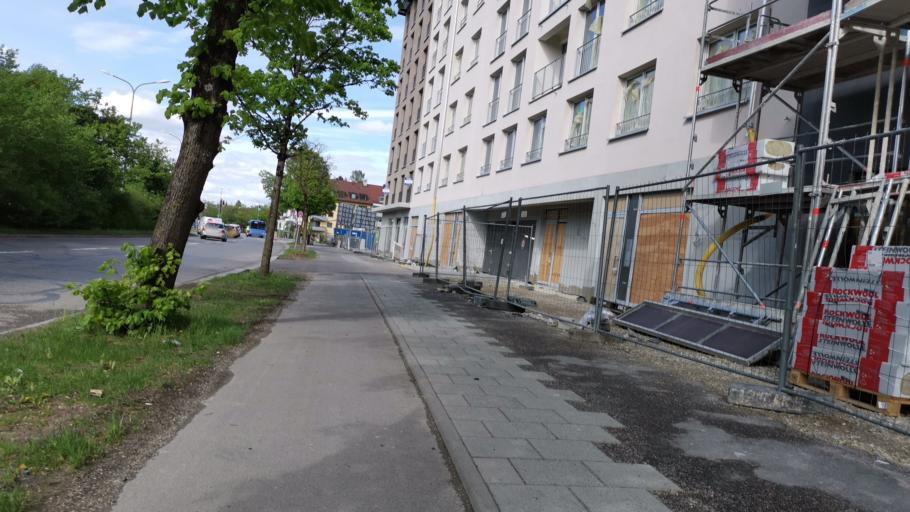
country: DE
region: Bavaria
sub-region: Upper Bavaria
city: Pullach im Isartal
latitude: 48.0969
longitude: 11.5076
